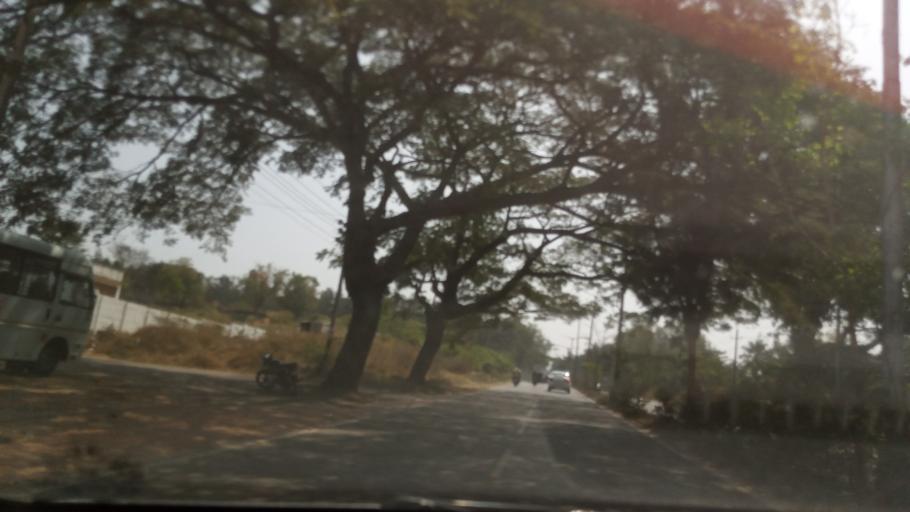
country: IN
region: Karnataka
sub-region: Mysore
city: Mysore
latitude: 12.3344
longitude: 76.6325
